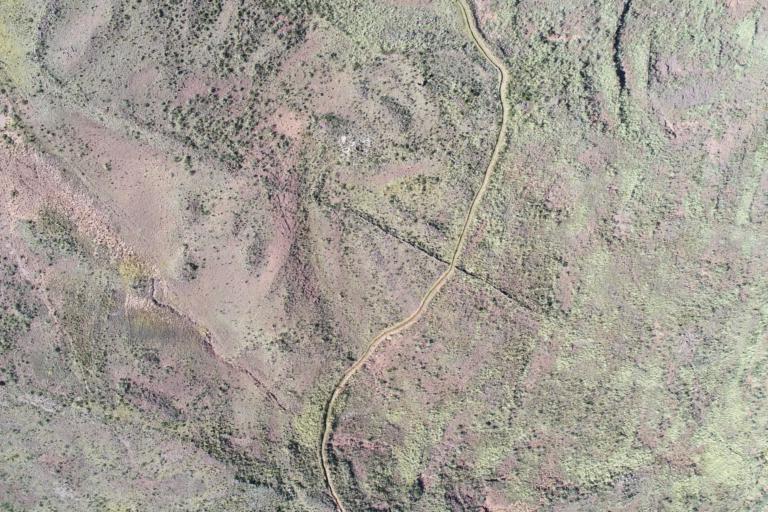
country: BO
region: La Paz
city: Tiahuanaco
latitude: -16.6031
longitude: -68.7576
